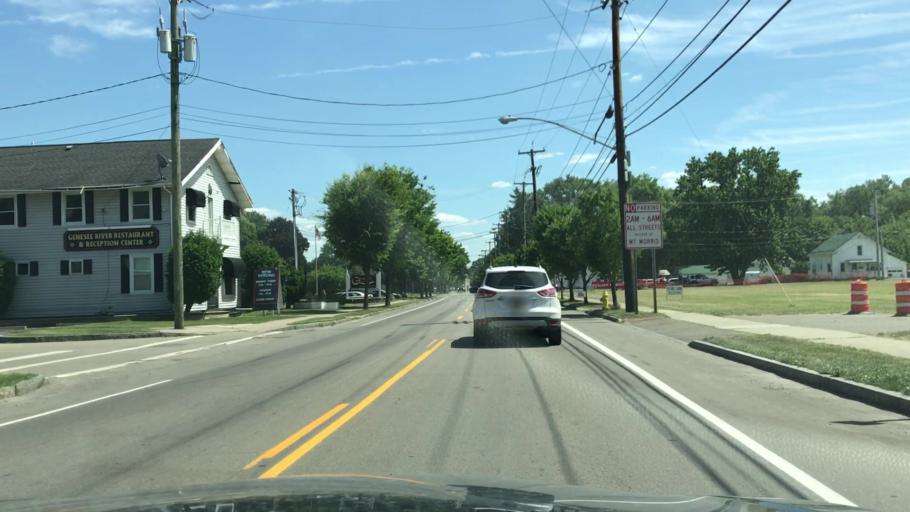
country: US
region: New York
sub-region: Livingston County
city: Mount Morris
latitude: 42.7374
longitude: -77.8811
